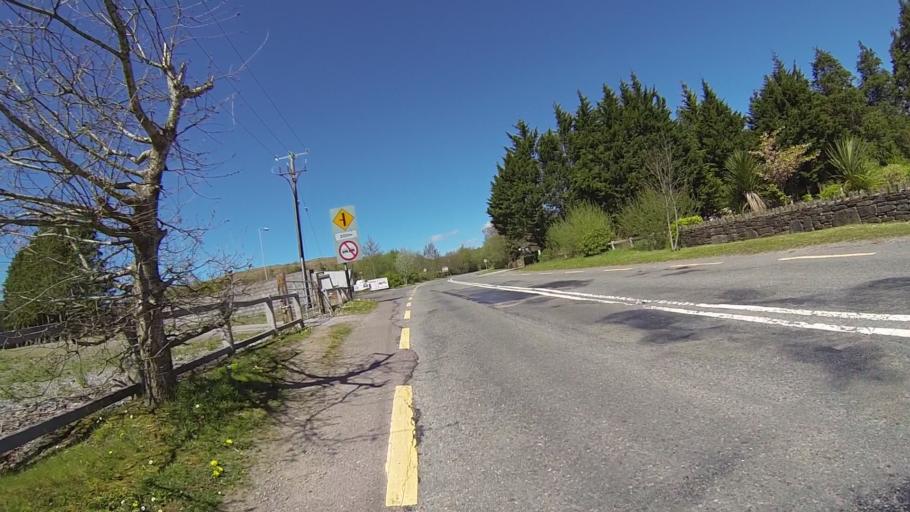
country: IE
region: Munster
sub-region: Ciarrai
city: Kenmare
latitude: 51.8863
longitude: -9.5959
